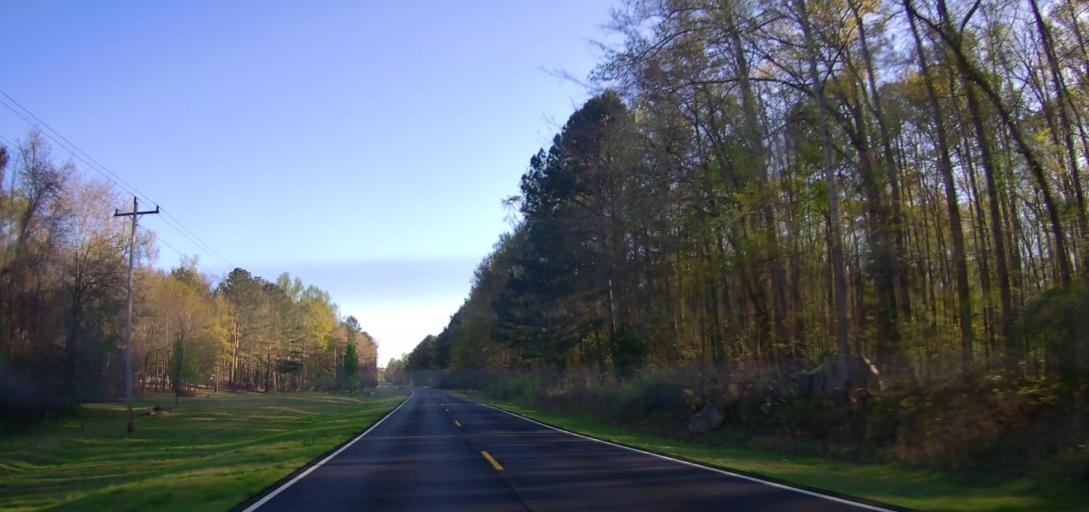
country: US
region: Georgia
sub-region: Butts County
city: Jackson
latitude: 33.3528
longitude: -83.9106
